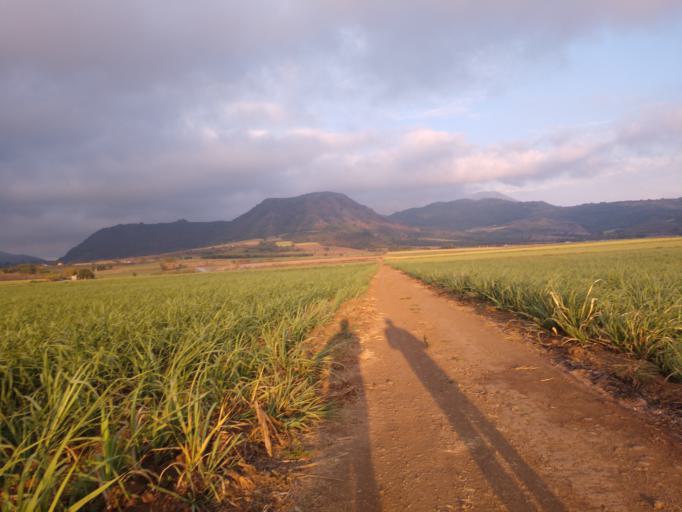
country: MX
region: Nayarit
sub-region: Tepic
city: La Corregidora
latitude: 21.4840
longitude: -104.8058
